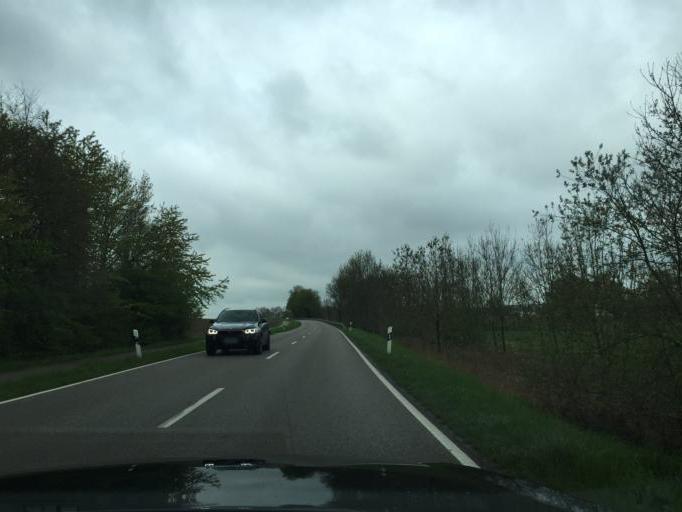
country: DE
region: Bavaria
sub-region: Swabia
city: Buttenwiesen
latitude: 48.5768
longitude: 10.7126
